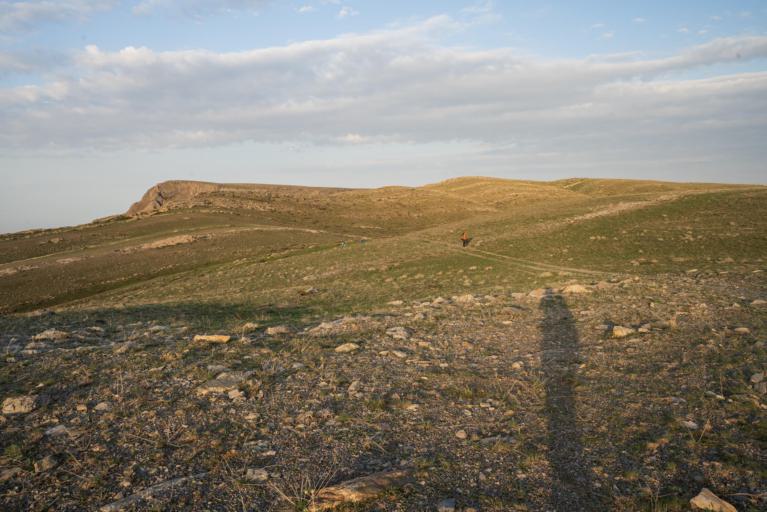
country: KZ
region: Ongtustik Qazaqstan
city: Kentau
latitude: 43.8924
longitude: 68.3506
